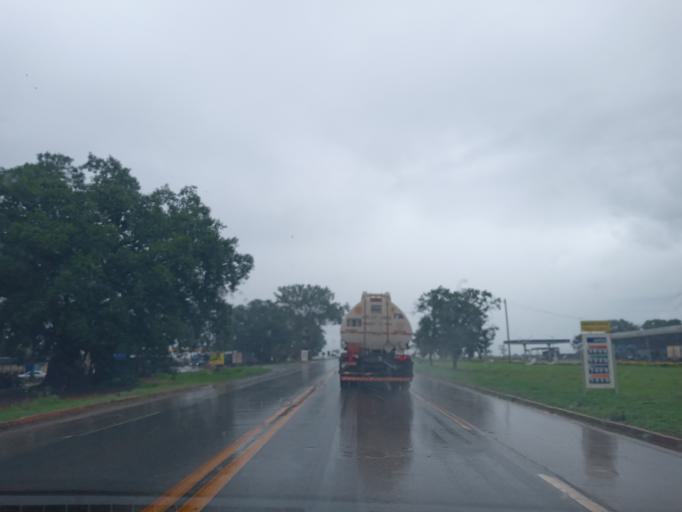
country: BR
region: Minas Gerais
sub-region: Luz
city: Luz
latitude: -19.7829
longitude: -45.6842
